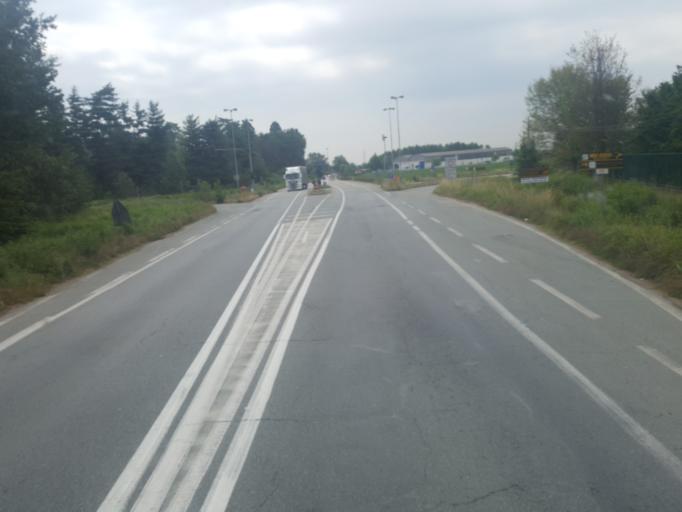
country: IT
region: Piedmont
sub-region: Provincia di Torino
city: Candiolo
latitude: 44.9664
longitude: 7.5703
